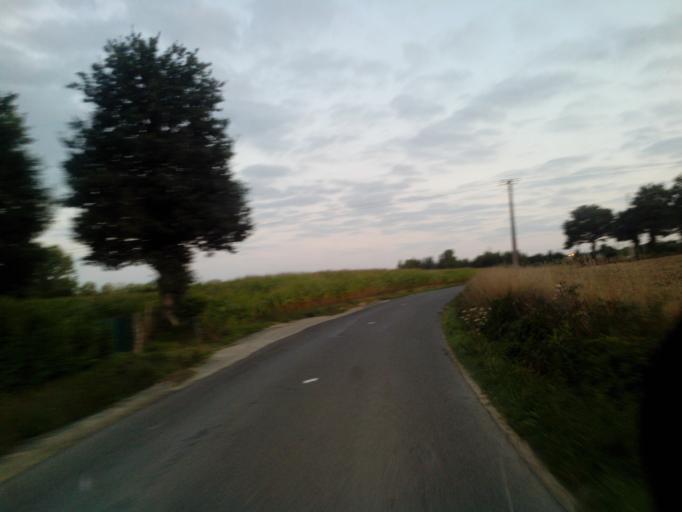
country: FR
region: Brittany
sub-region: Departement d'Ille-et-Vilaine
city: Montfort-sur-Meu
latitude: 48.1494
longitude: -1.9667
